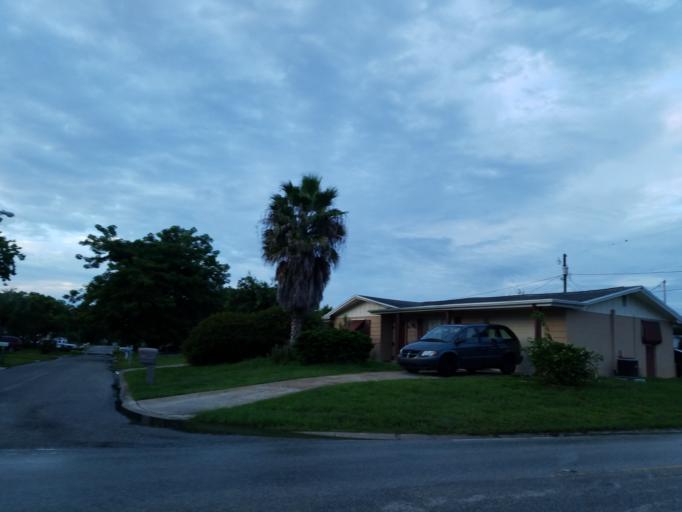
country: US
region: Florida
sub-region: Pasco County
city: Beacon Square
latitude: 28.2095
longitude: -82.7540
